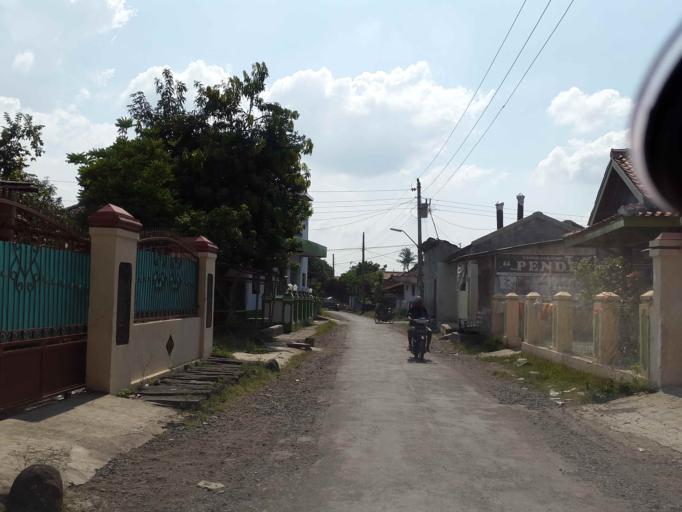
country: ID
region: Central Java
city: Dukuhturi
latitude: -6.9674
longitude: 109.0559
